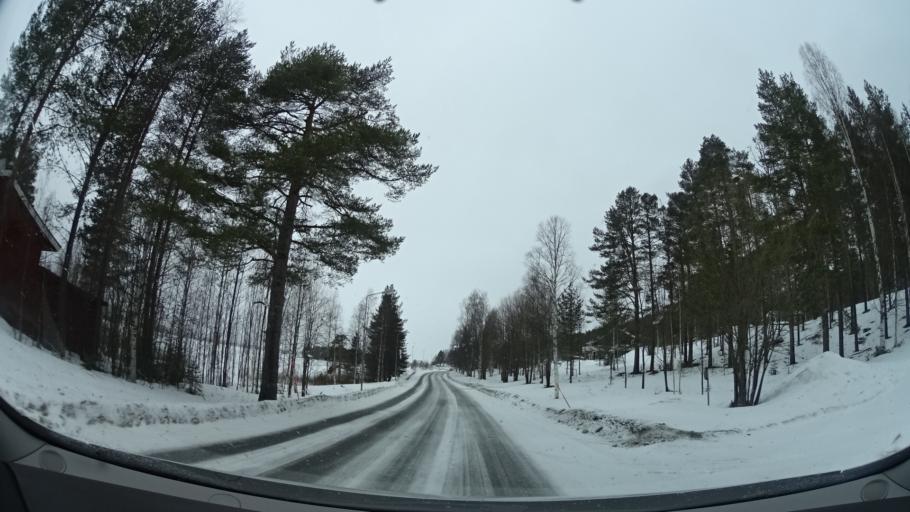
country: SE
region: Vaesterbotten
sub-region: Mala Kommun
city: Mala
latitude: 65.1731
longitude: 18.7588
